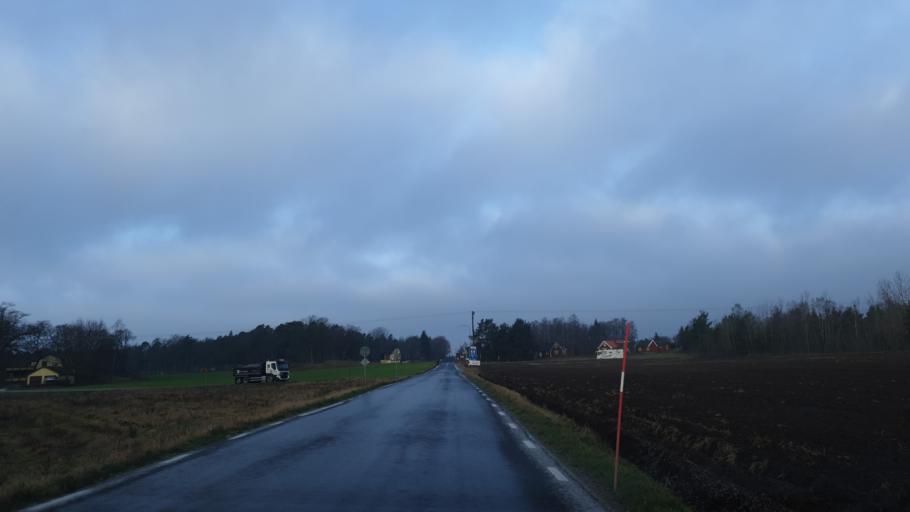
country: SE
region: Blekinge
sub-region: Karlshamns Kommun
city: Morrum
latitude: 56.1691
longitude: 14.7442
